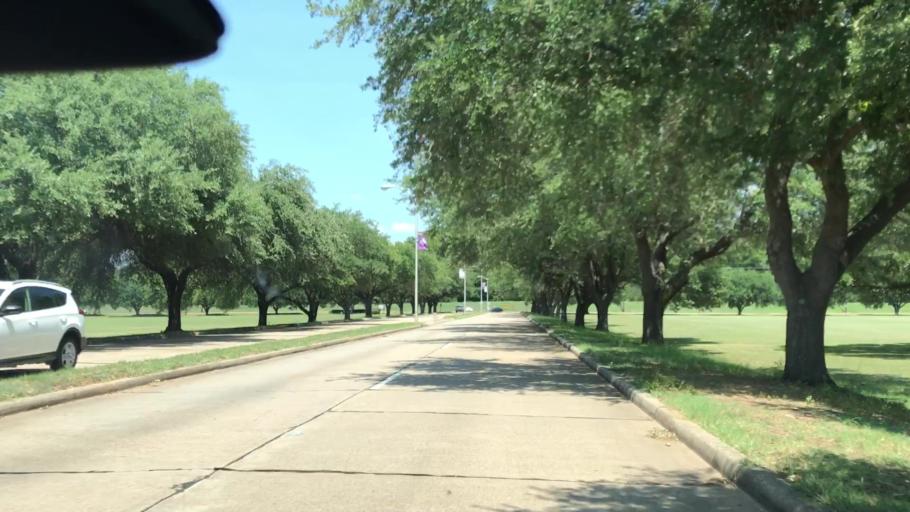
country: US
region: Louisiana
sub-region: Bossier Parish
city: Bossier City
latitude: 32.4274
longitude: -93.6992
